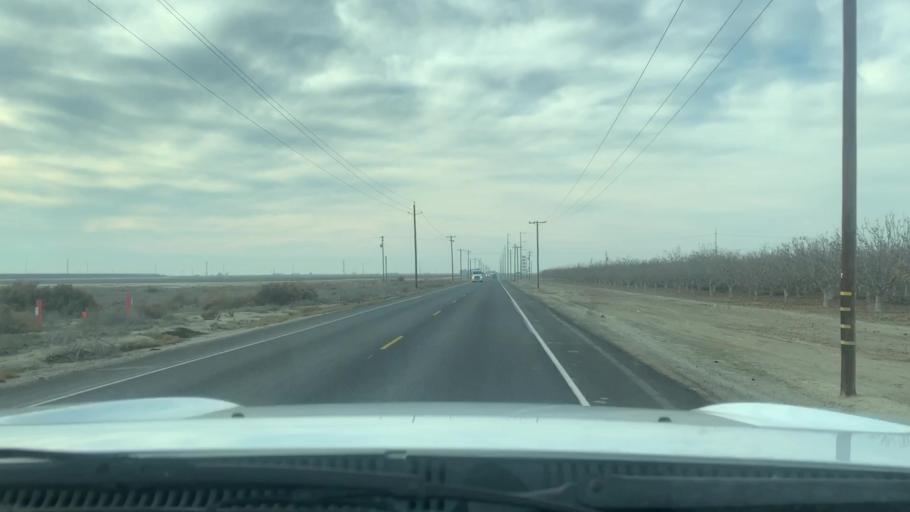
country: US
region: California
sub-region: Kern County
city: Buttonwillow
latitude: 35.4423
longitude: -119.4360
